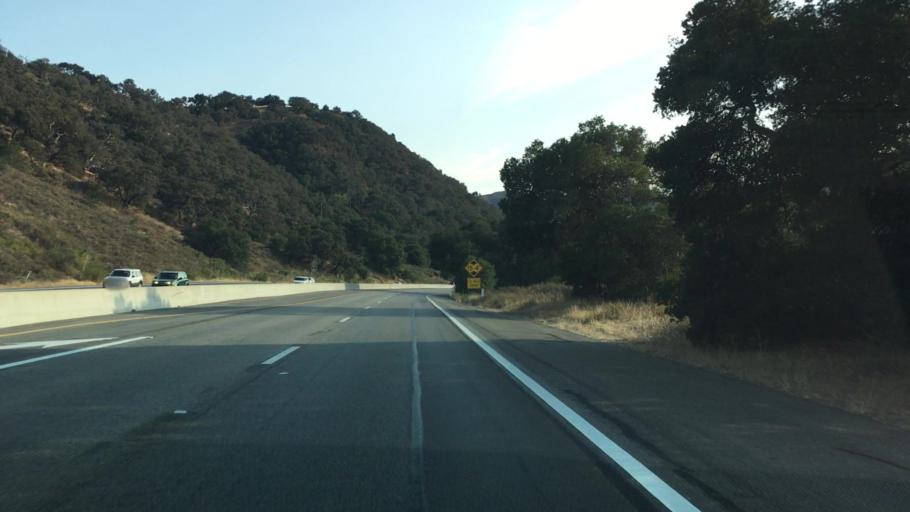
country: US
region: California
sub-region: Santa Barbara County
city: Buellton
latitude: 34.5168
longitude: -120.2181
